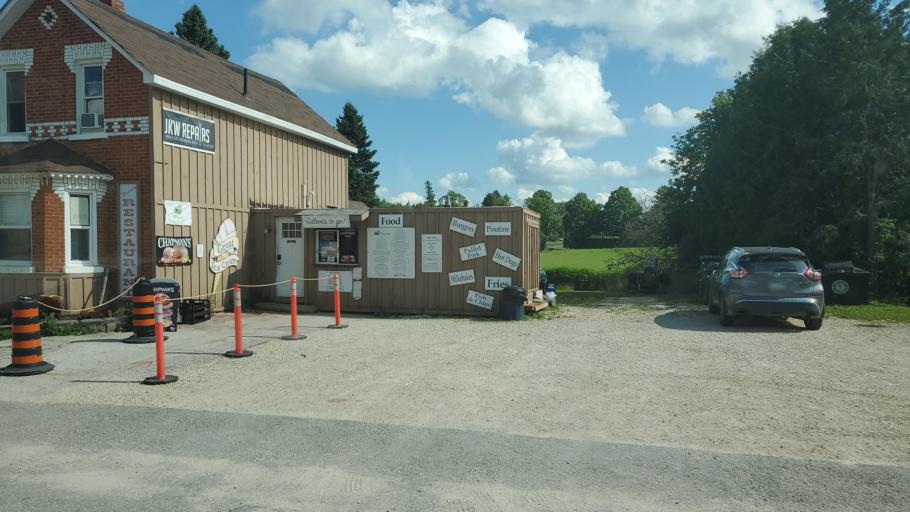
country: CA
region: Ontario
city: Collingwood
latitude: 44.3093
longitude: -80.3977
